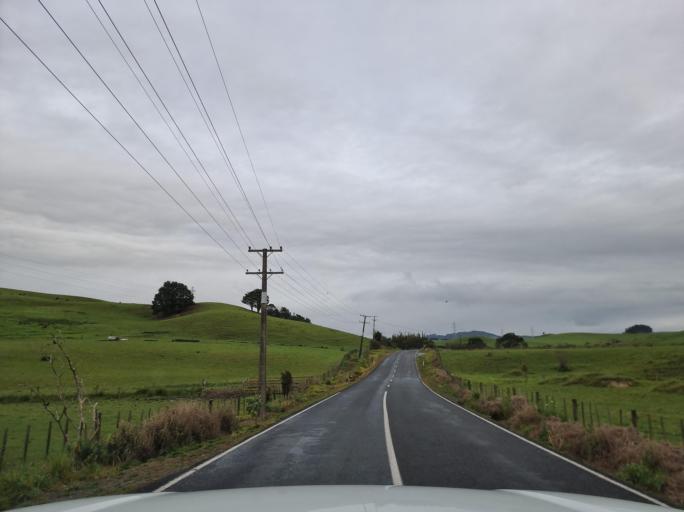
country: NZ
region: Northland
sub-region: Whangarei
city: Ruakaka
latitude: -35.9731
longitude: 174.4302
